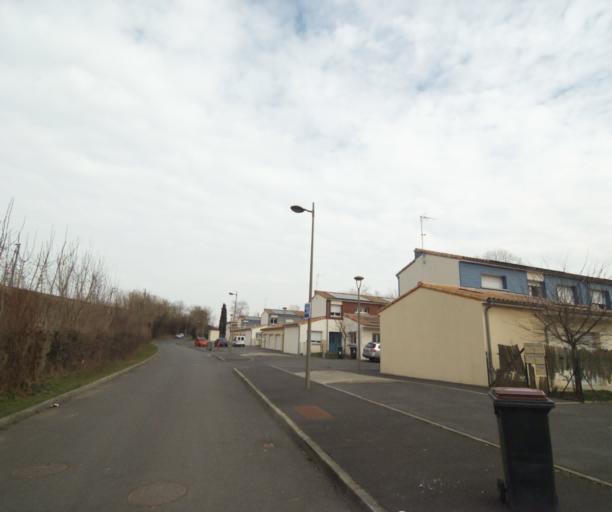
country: FR
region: Poitou-Charentes
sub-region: Departement des Deux-Sevres
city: Niort
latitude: 46.3031
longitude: -0.4672
